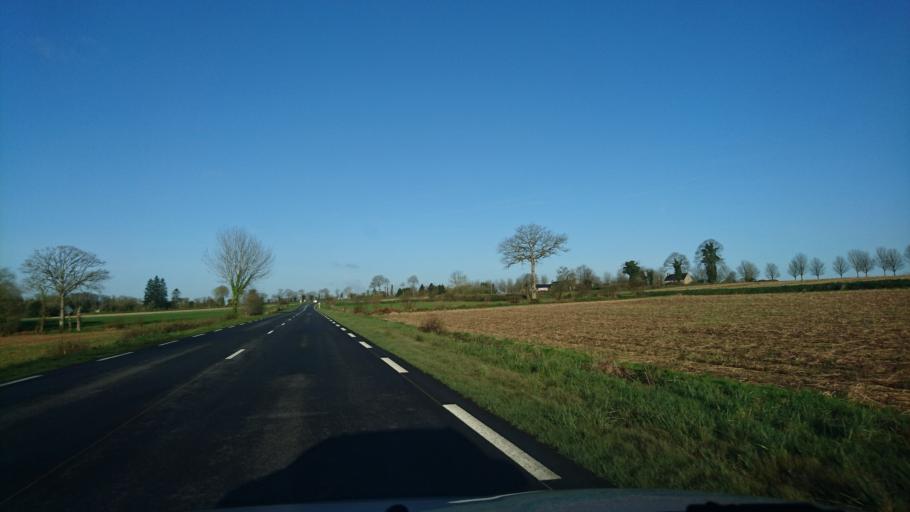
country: FR
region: Brittany
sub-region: Departement d'Ille-et-Vilaine
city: La Boussac
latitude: 48.4954
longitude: -1.6107
